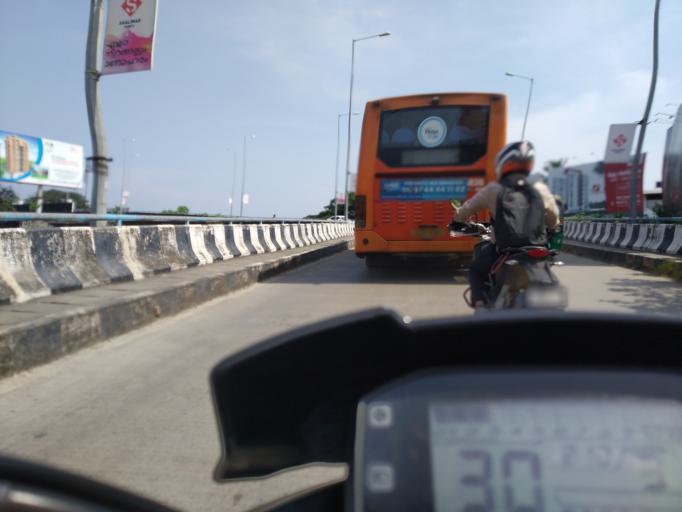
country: IN
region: Kerala
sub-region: Ernakulam
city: Cochin
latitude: 9.9768
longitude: 76.2888
